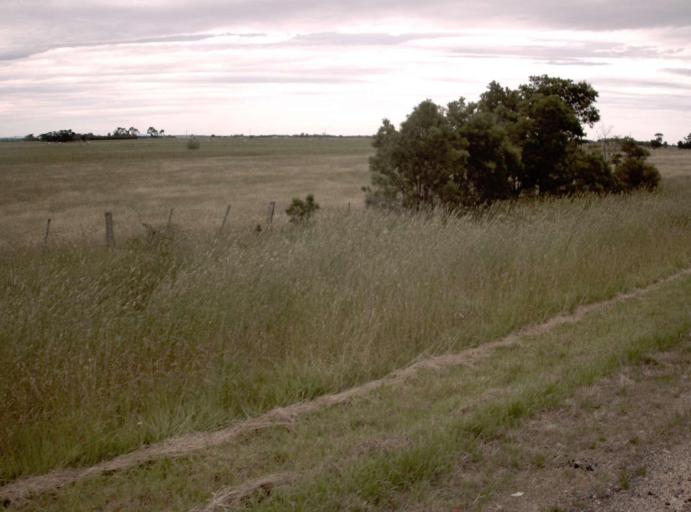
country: AU
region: Victoria
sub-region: Wellington
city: Sale
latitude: -38.0720
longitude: 147.1061
